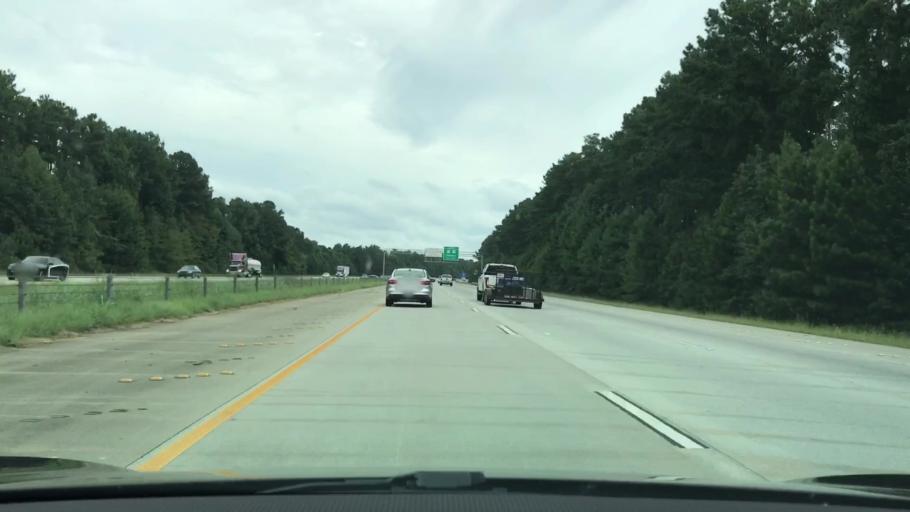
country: US
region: Georgia
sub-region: Coweta County
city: East Newnan
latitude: 33.3073
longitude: -84.7897
